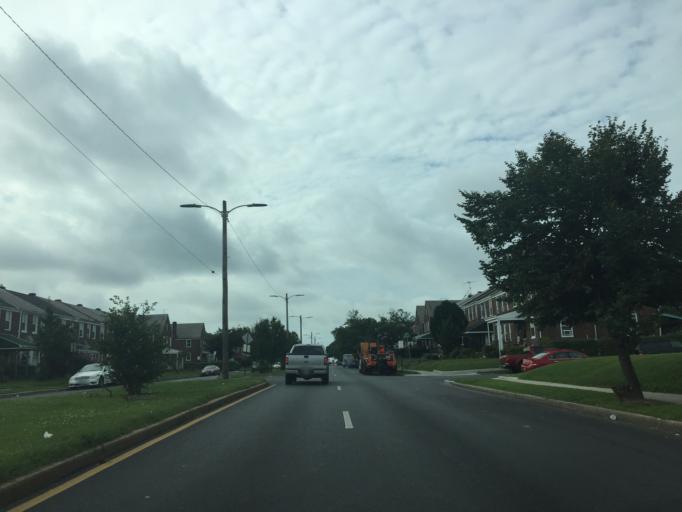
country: US
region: Maryland
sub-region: City of Baltimore
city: Baltimore
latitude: 39.3187
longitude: -76.5706
